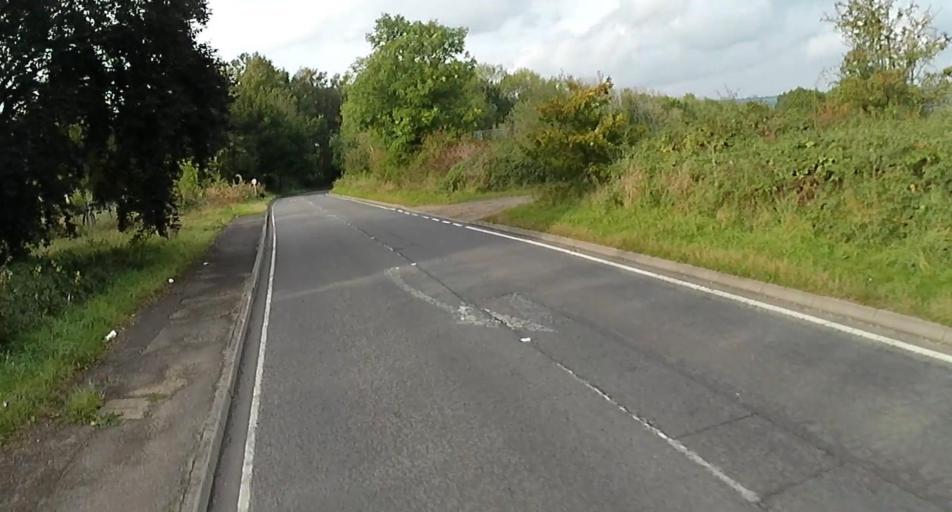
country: GB
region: England
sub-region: West Berkshire
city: Thatcham
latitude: 51.3815
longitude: -1.2483
